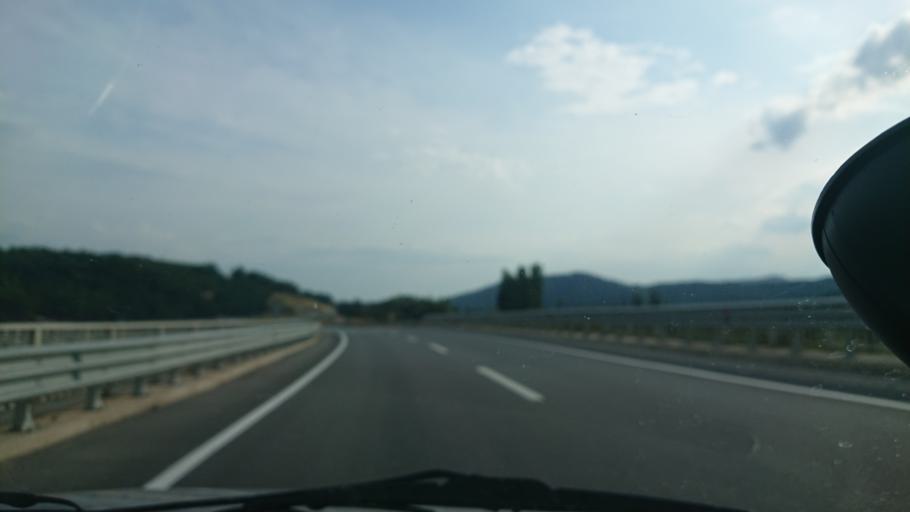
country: TR
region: Kuetahya
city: Gediz
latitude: 38.9294
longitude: 29.3050
